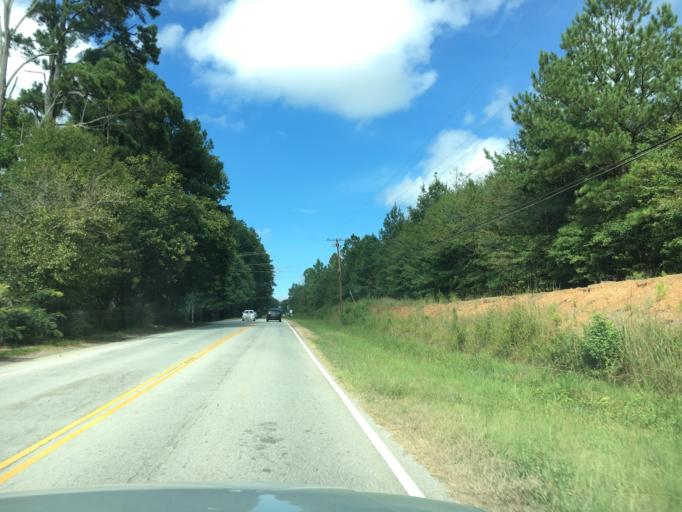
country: US
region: South Carolina
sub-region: Spartanburg County
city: Inman
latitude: 35.0562
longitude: -82.0841
